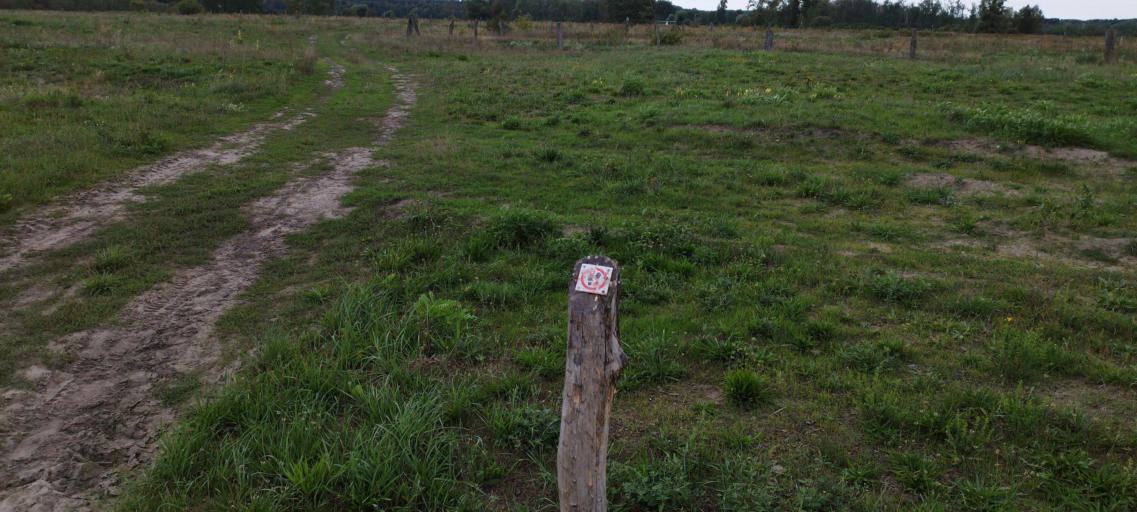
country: DE
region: Brandenburg
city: Dallgow-Doeberitz
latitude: 52.4998
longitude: 13.0174
